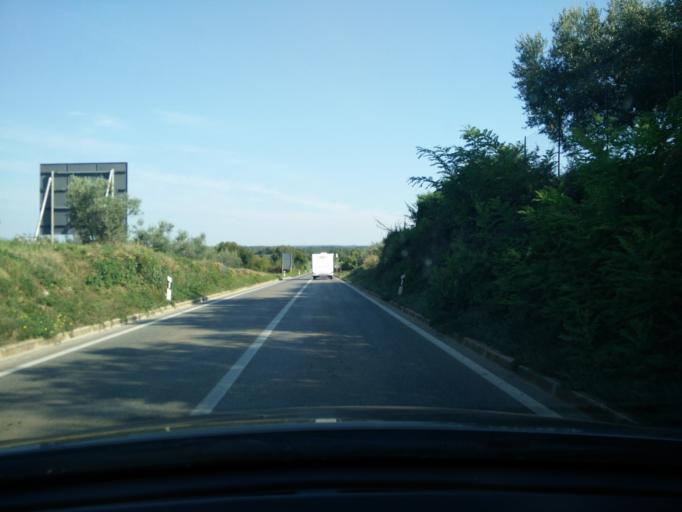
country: HR
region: Istarska
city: Novigrad
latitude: 45.3021
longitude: 13.6224
